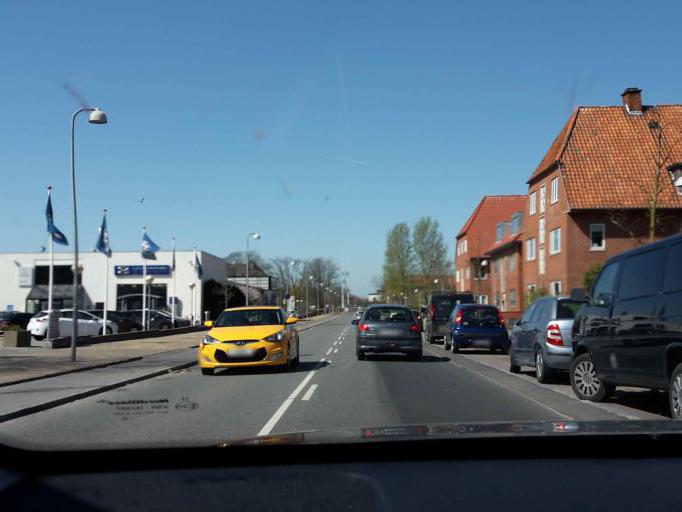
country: DK
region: South Denmark
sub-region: Odense Kommune
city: Odense
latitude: 55.3945
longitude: 10.3561
